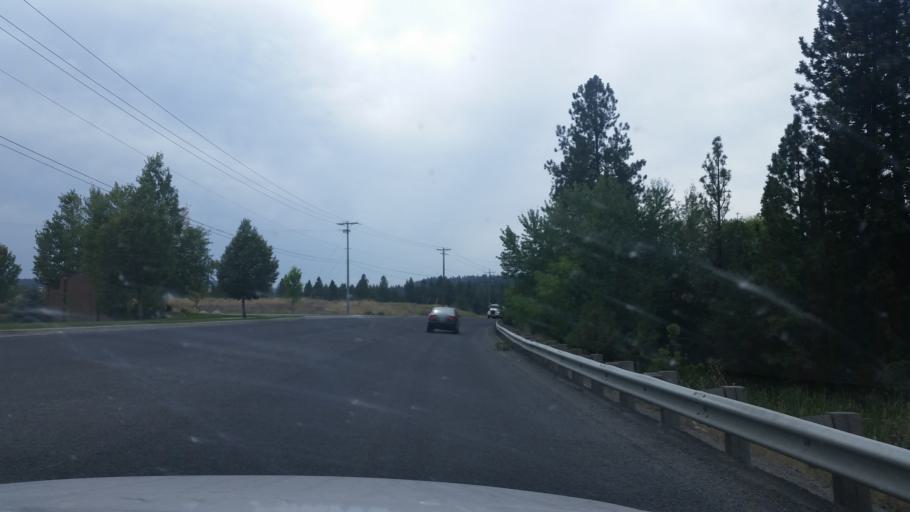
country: US
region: Washington
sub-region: Spokane County
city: Spokane
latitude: 47.6666
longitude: -117.4695
